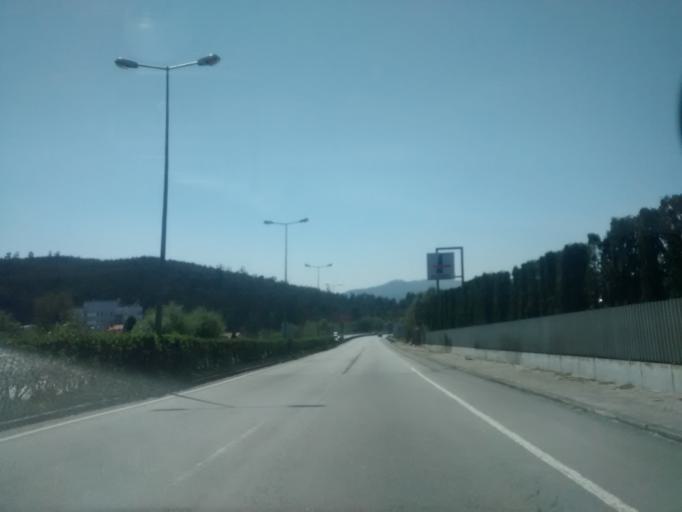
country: PT
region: Braga
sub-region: Braga
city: Braga
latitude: 41.5282
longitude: -8.4140
